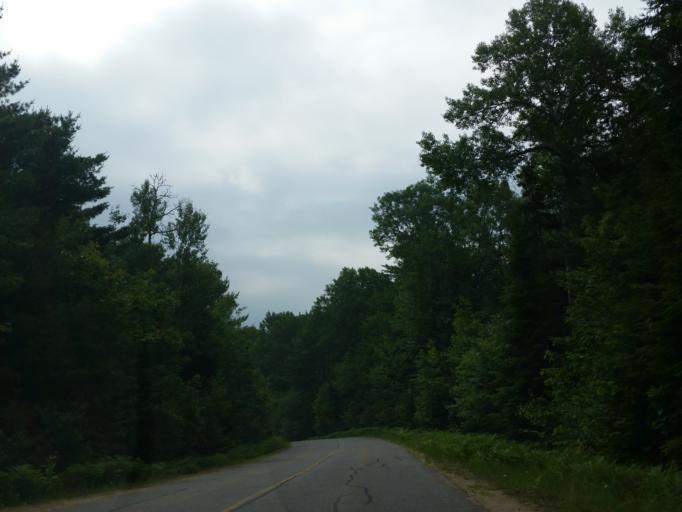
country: CA
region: Ontario
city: Bancroft
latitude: 45.5869
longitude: -78.3633
